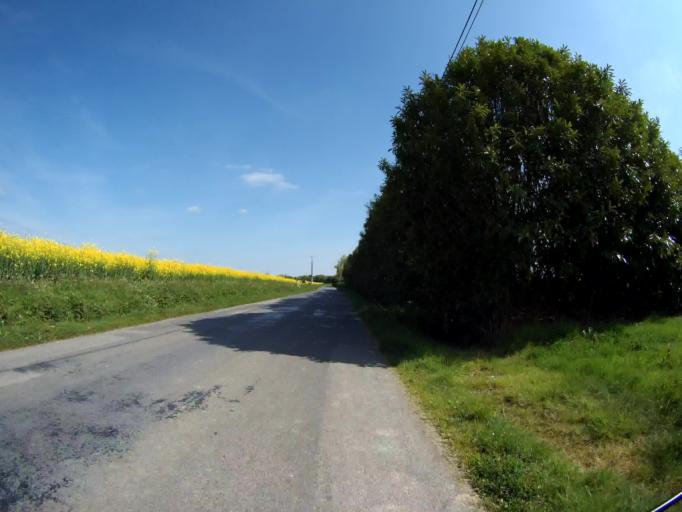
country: FR
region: Brittany
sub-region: Departement d'Ille-et-Vilaine
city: Saint-Erblon
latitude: 48.0227
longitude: -1.6361
